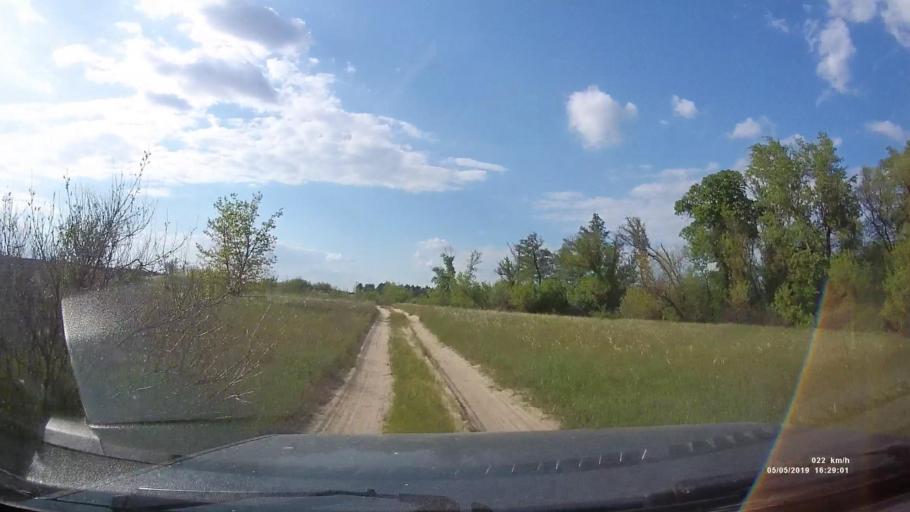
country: RU
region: Rostov
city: Ust'-Donetskiy
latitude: 47.7693
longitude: 41.0151
